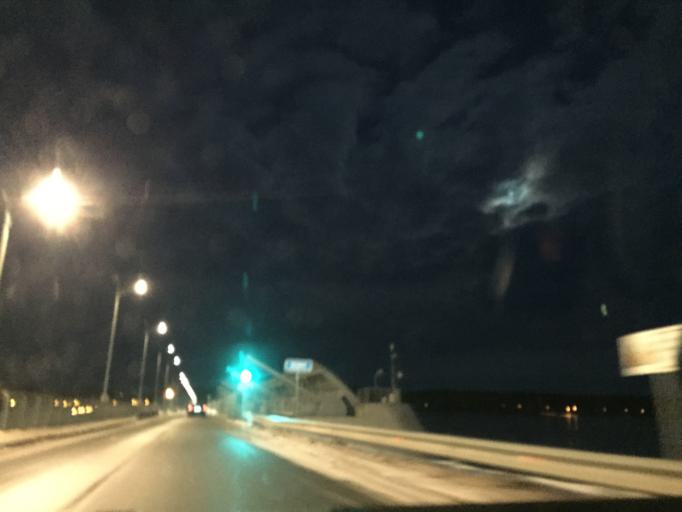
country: LV
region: Kegums
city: Kegums
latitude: 56.7387
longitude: 24.7071
